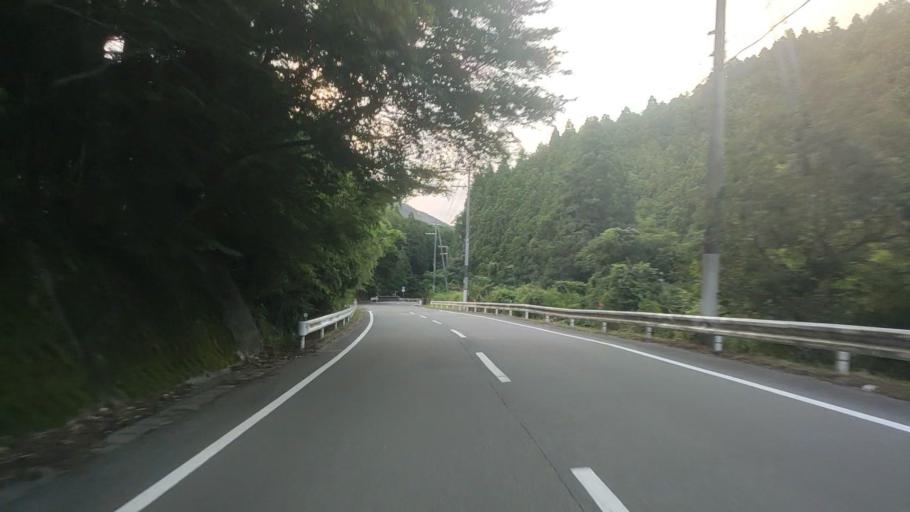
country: JP
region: Wakayama
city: Tanabe
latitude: 33.8257
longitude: 135.6361
